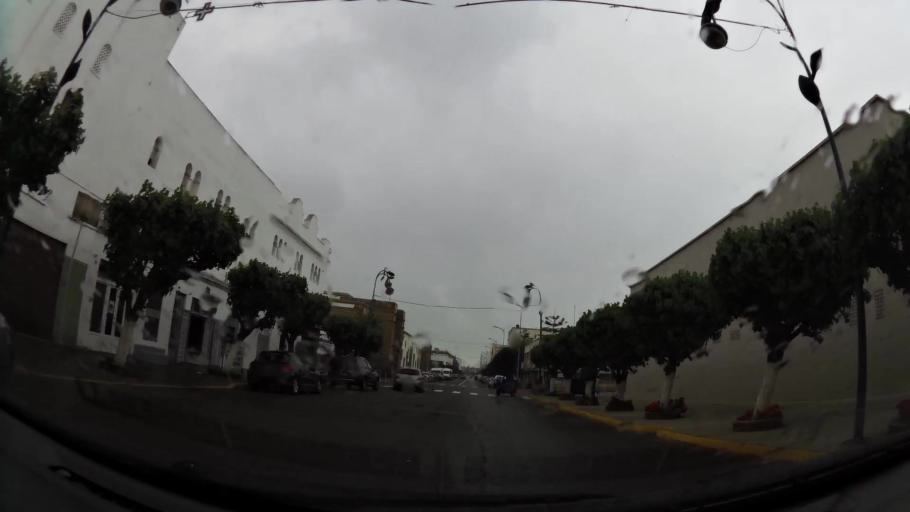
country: MA
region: Grand Casablanca
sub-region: Casablanca
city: Casablanca
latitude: 33.5793
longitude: -7.6056
